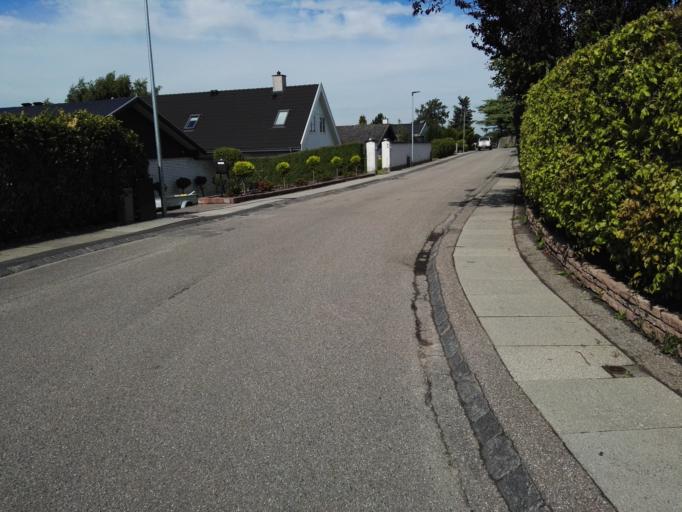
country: DK
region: Capital Region
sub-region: Egedal Kommune
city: Olstykke
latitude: 55.7933
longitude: 12.1381
